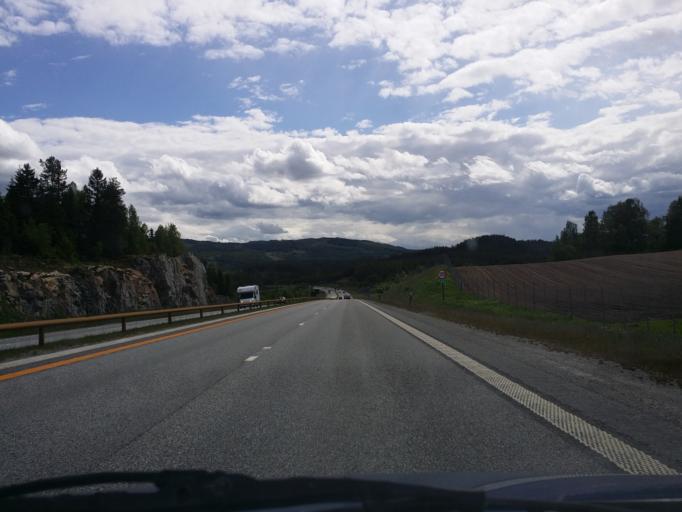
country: NO
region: Hedmark
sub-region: Stange
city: Stange
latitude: 60.6283
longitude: 11.2997
